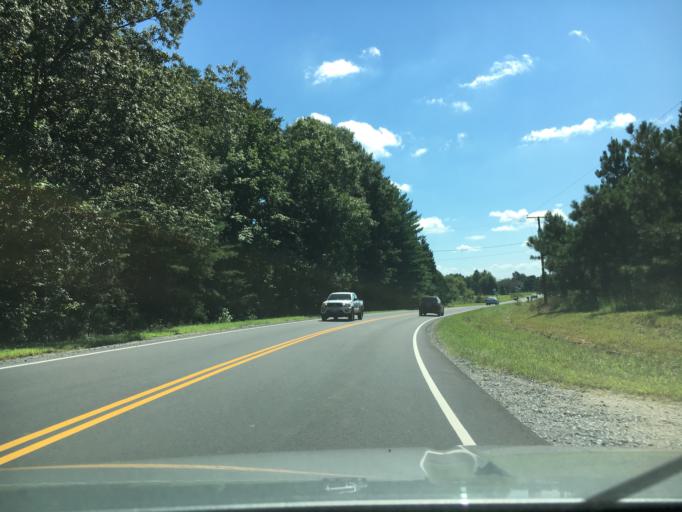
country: US
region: Virginia
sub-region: Amelia County
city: Amelia Court House
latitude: 37.3801
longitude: -77.9003
